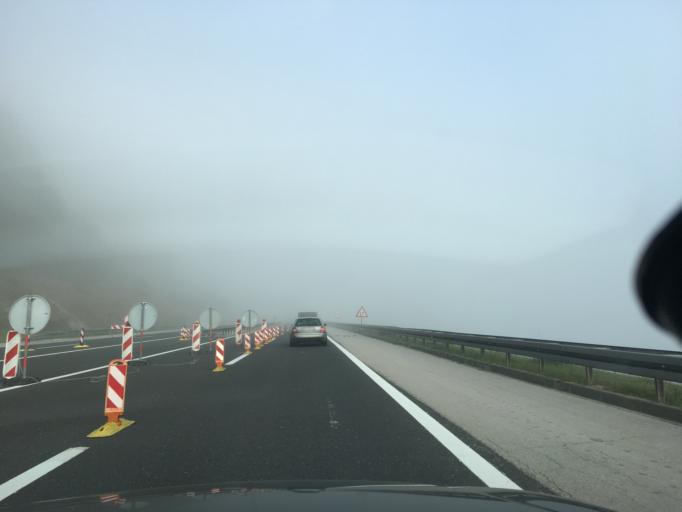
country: HR
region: Licko-Senjska
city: Otocac
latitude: 44.8528
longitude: 15.2272
